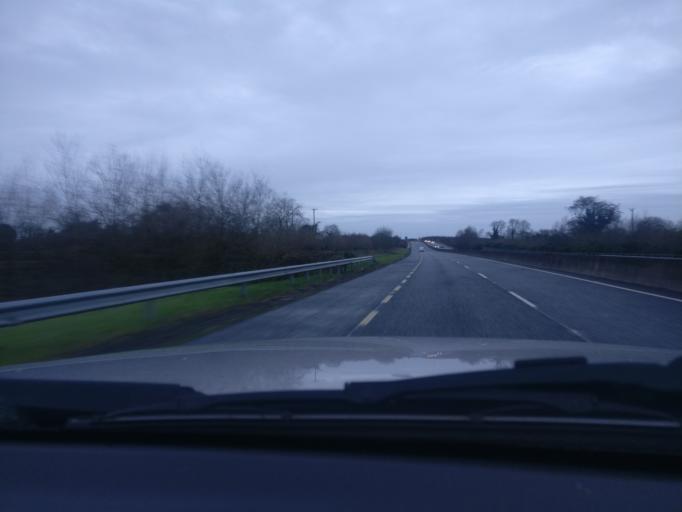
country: IE
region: Leinster
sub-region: An Mhi
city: Navan
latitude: 53.6435
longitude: -6.7308
